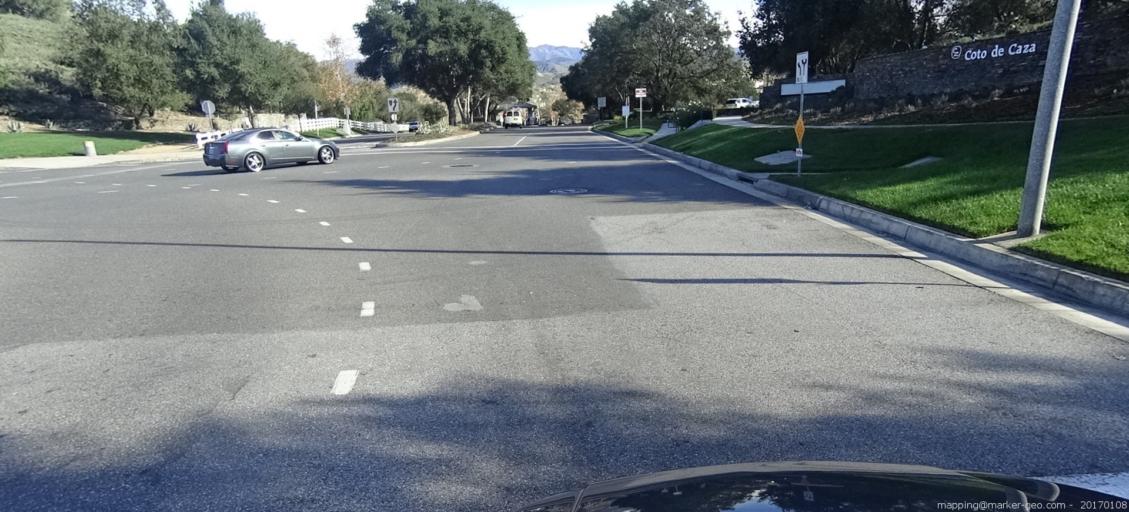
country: US
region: California
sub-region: Orange County
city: Coto De Caza
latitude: 33.5737
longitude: -117.5909
